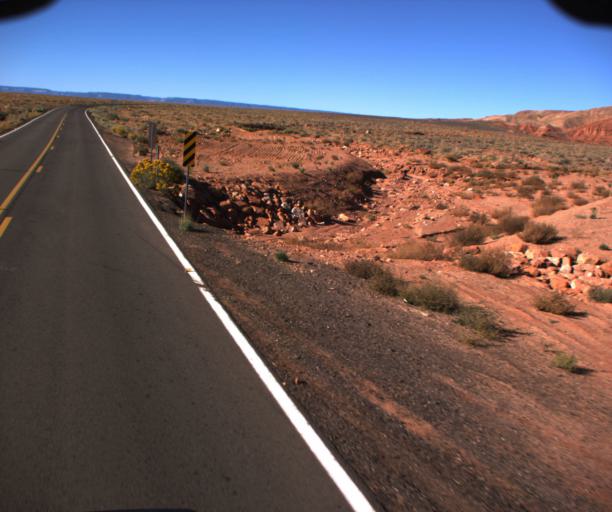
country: US
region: Arizona
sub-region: Coconino County
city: LeChee
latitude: 36.7067
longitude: -111.7847
